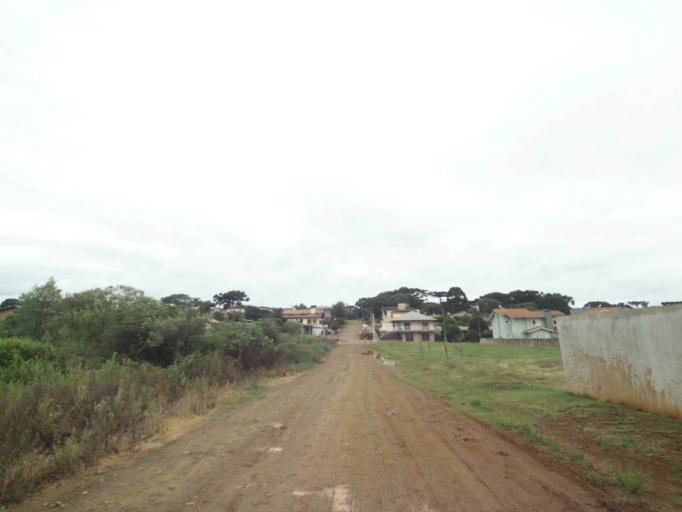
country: BR
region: Rio Grande do Sul
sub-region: Lagoa Vermelha
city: Lagoa Vermelha
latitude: -28.2161
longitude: -51.5239
